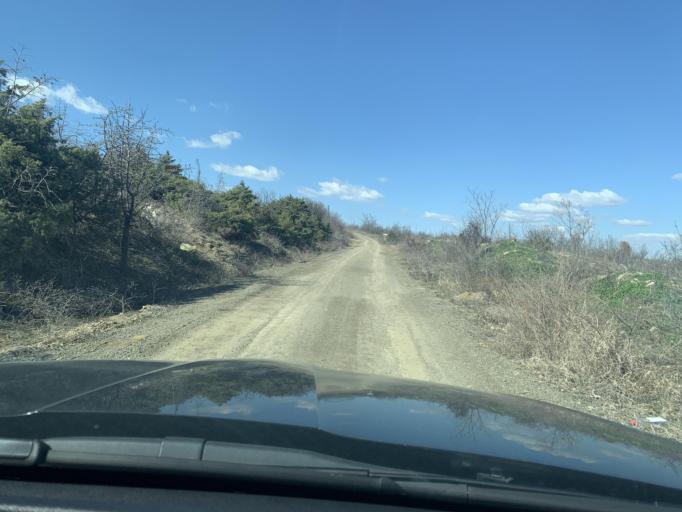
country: MK
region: Demir Kapija
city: Demir Kapija
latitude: 41.4124
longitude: 22.2241
